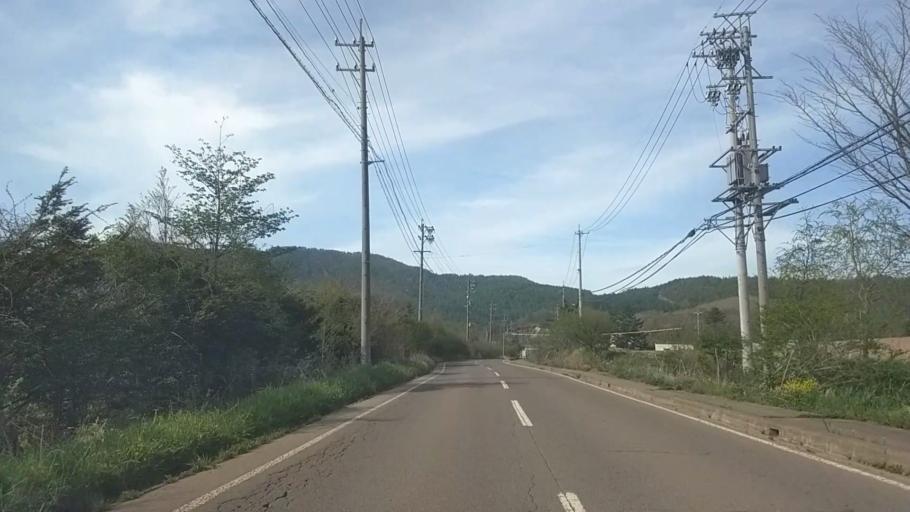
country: JP
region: Yamanashi
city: Nirasaki
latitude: 35.9436
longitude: 138.4686
